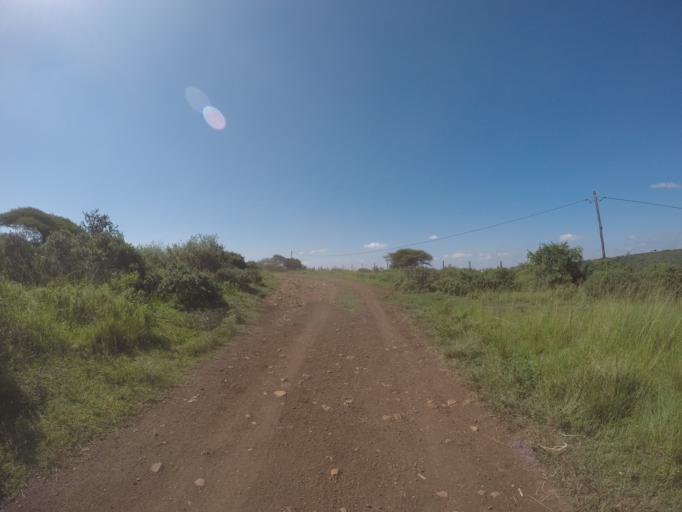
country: ZA
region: KwaZulu-Natal
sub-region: uThungulu District Municipality
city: Empangeni
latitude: -28.5691
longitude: 31.7002
